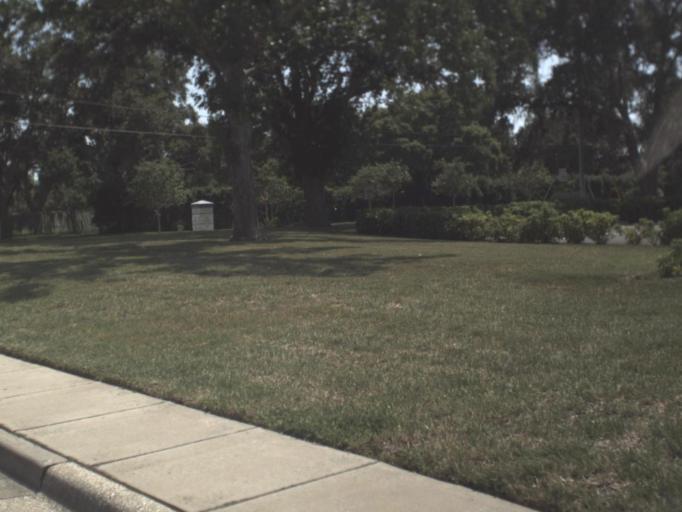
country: US
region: Florida
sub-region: Pinellas County
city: Gulfport
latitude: 27.7415
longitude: -82.6794
